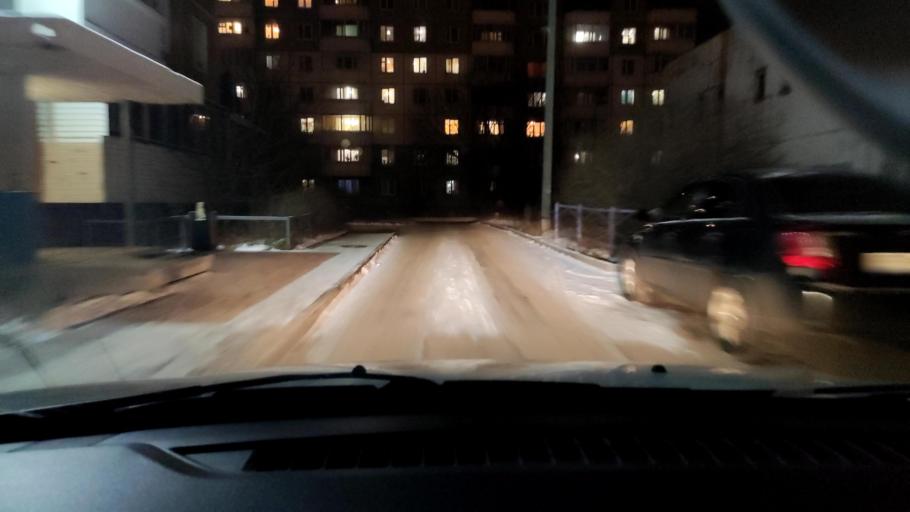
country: RU
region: Perm
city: Overyata
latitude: 58.0129
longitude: 55.9595
